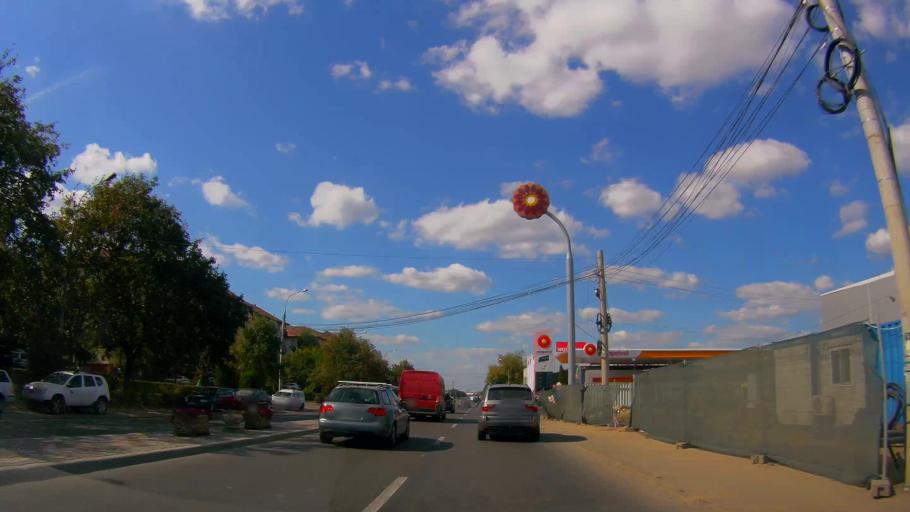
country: RO
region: Salaj
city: Zalau
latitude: 47.2011
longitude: 23.0548
